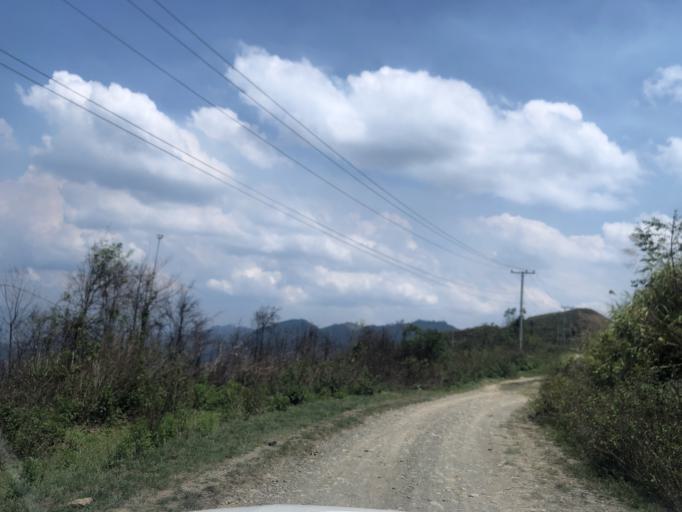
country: LA
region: Phongsali
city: Phongsali
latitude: 21.4146
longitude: 102.1857
